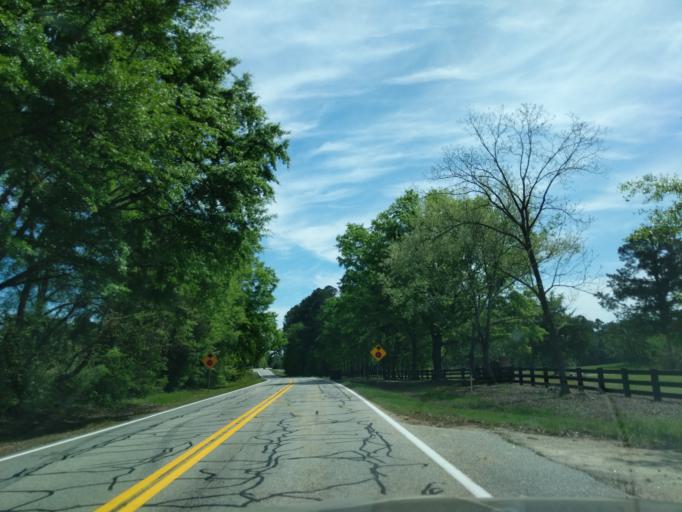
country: US
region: Georgia
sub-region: Columbia County
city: Appling
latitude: 33.6104
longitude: -82.3313
